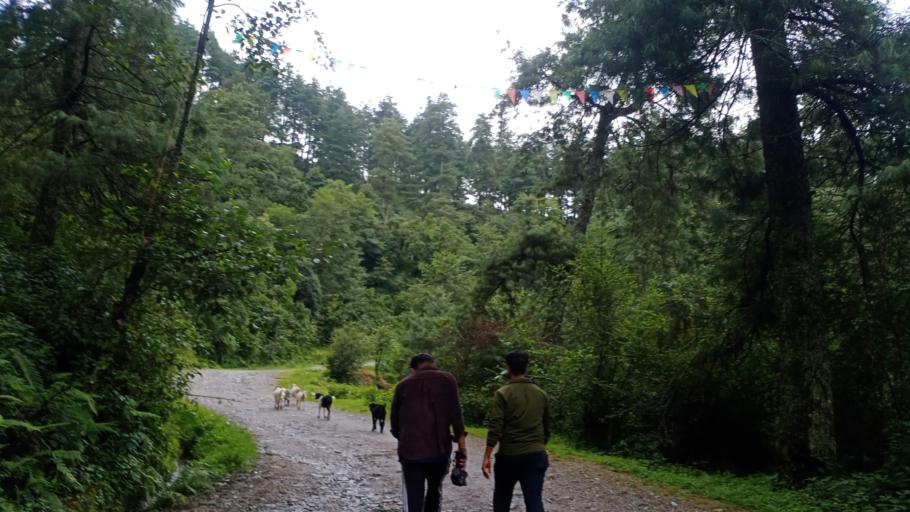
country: NP
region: Central Region
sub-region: Janakpur Zone
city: Ramechhap
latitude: 27.6307
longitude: 86.2345
